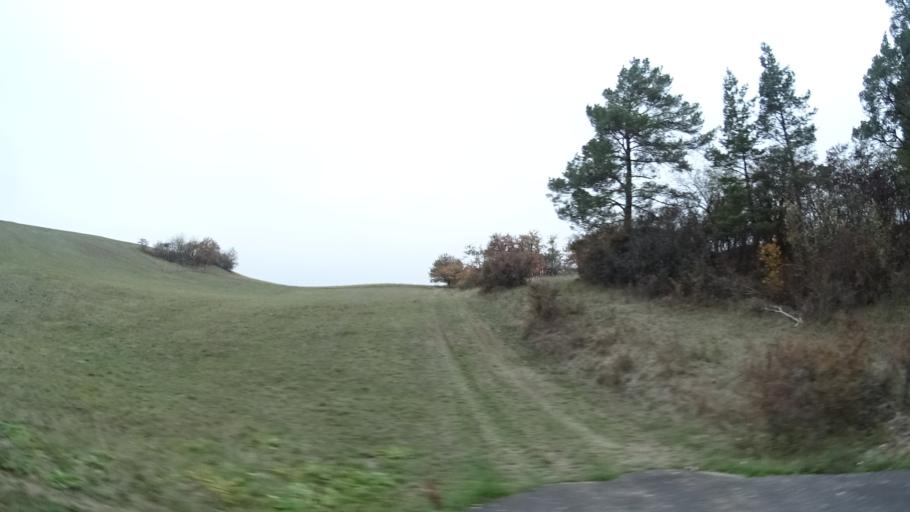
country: DE
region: Thuringia
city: Erbenhausen
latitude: 50.5884
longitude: 10.1450
